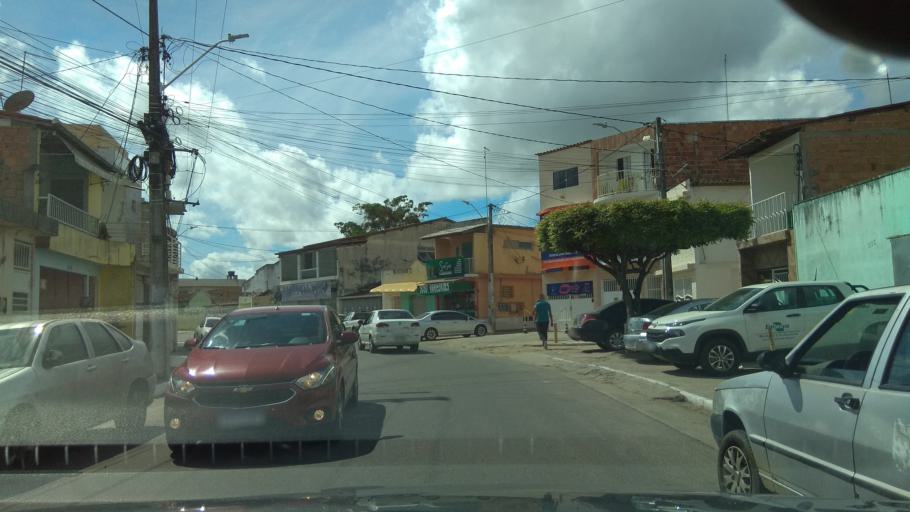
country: BR
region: Bahia
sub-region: Santo Antonio De Jesus
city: Santo Antonio de Jesus
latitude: -12.9794
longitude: -39.2751
